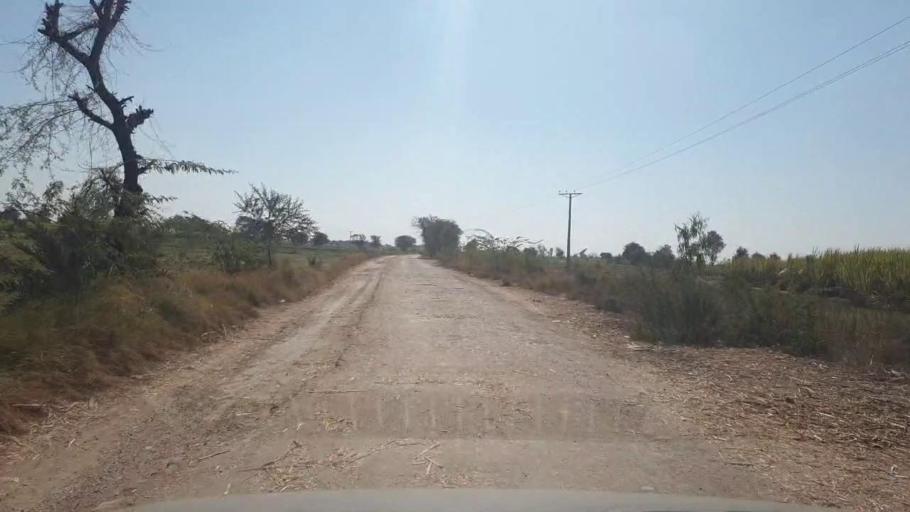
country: PK
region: Sindh
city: Mirwah Gorchani
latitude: 25.3073
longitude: 69.1157
